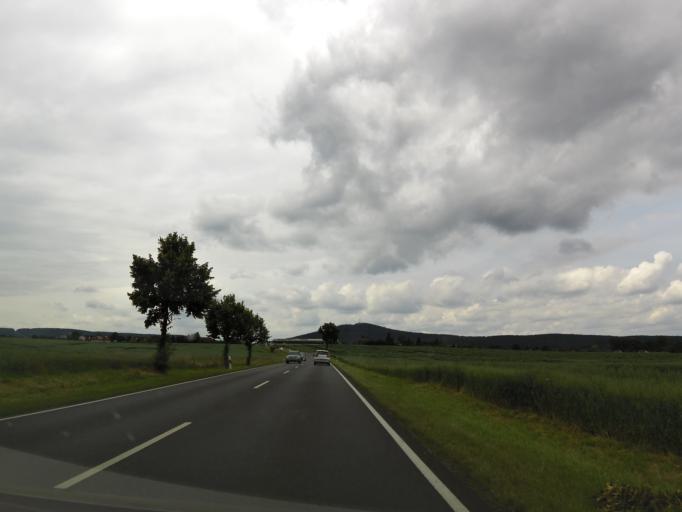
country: DE
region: Thuringia
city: Tiefenort
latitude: 50.8240
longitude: 10.1716
